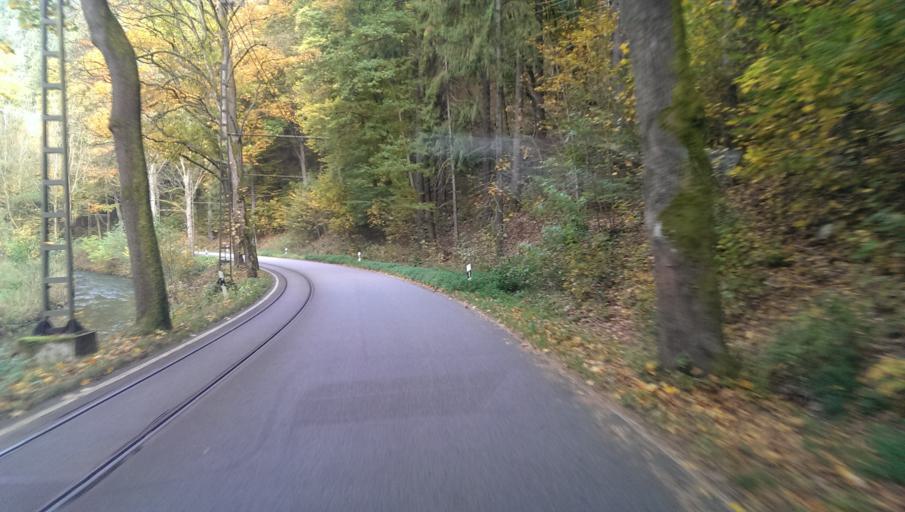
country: DE
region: Saxony
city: Bad Schandau
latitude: 50.9297
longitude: 14.2161
